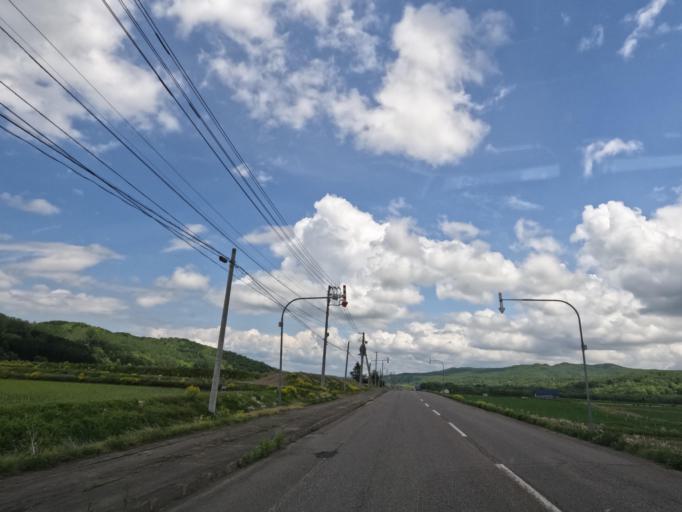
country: JP
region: Hokkaido
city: Takikawa
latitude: 43.5905
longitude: 141.7563
